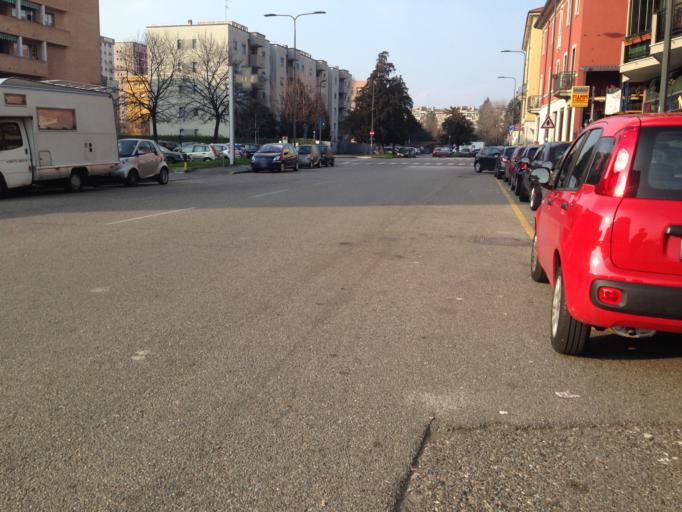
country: IT
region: Lombardy
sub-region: Citta metropolitana di Milano
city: Cesano Boscone
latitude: 45.4710
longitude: 9.1094
